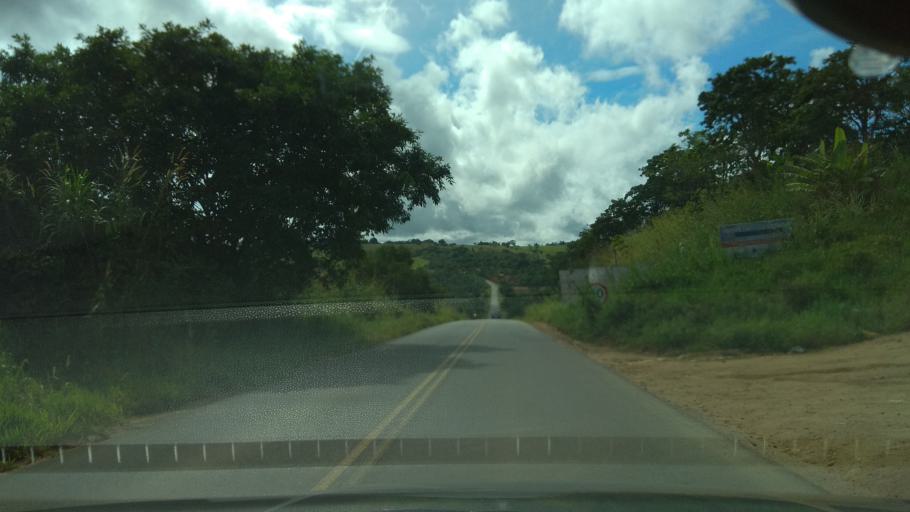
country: BR
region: Bahia
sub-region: Mutuipe
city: Mutuipe
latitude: -13.2286
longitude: -39.4919
